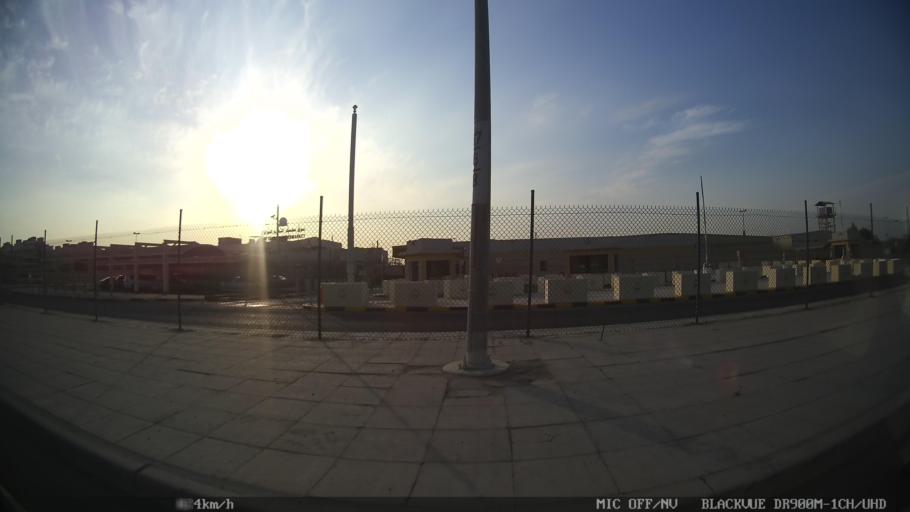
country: KW
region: Mubarak al Kabir
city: Sabah as Salim
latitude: 29.2604
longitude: 48.0211
